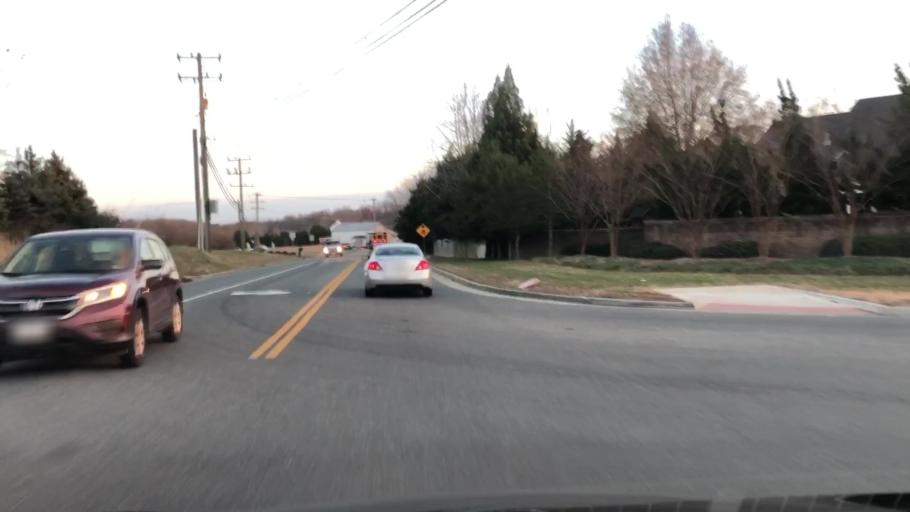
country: US
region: Virginia
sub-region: Stafford County
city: Falmouth
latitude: 38.3681
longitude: -77.4876
